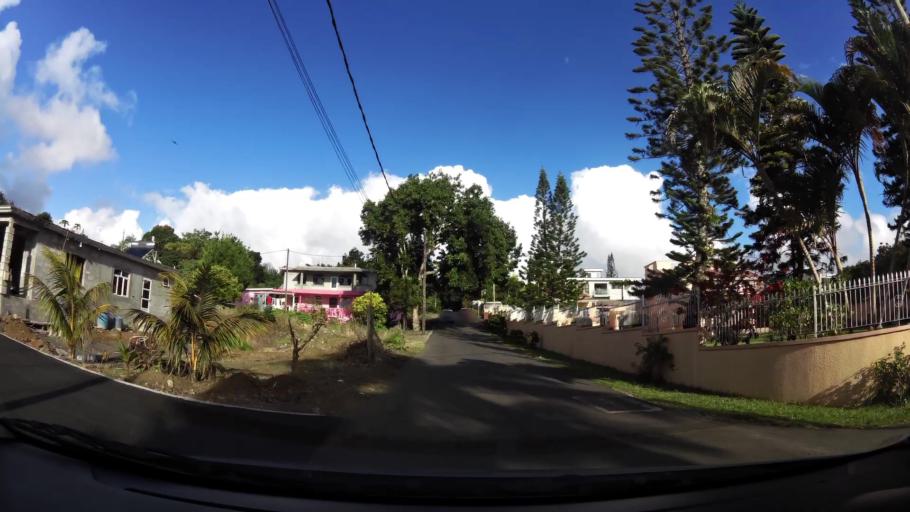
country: MU
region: Plaines Wilhems
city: Curepipe
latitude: -20.3089
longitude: 57.4996
